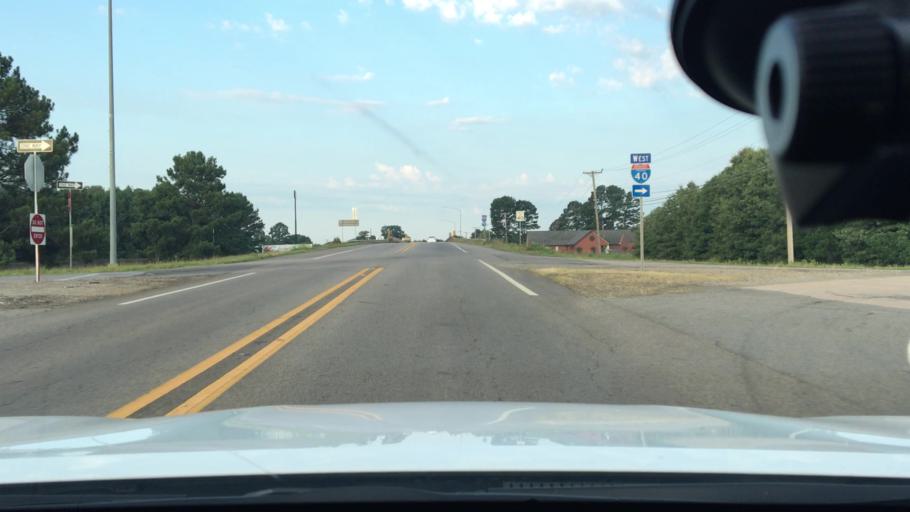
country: US
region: Arkansas
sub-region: Johnson County
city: Clarksville
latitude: 35.4676
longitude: -93.5209
